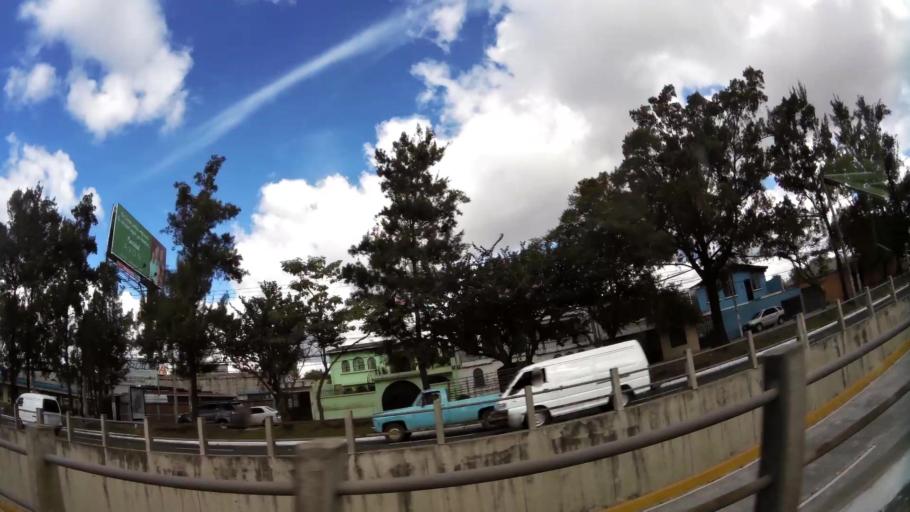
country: GT
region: Guatemala
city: Guatemala City
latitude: 14.6167
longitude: -90.5551
